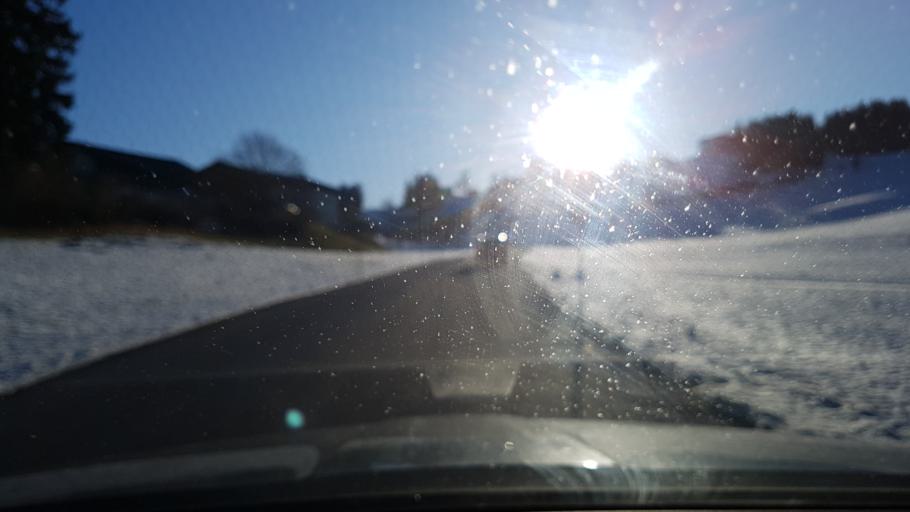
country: AT
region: Salzburg
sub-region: Politischer Bezirk Hallein
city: Kuchl
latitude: 47.6583
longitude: 13.1878
